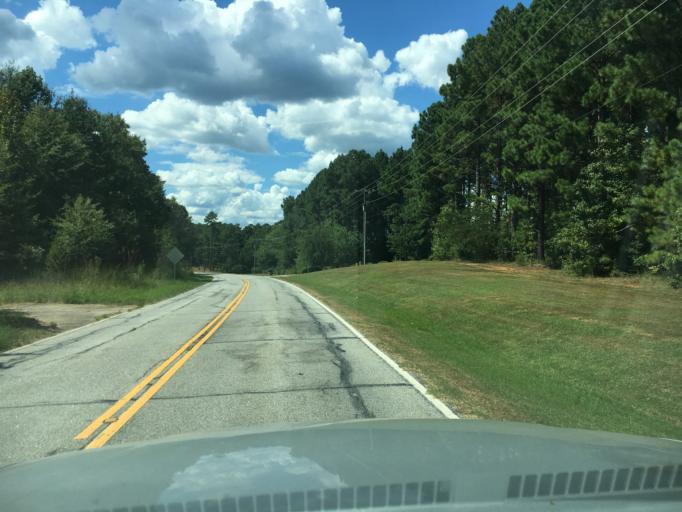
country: US
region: South Carolina
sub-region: Laurens County
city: Laurens
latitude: 34.5169
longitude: -82.0978
